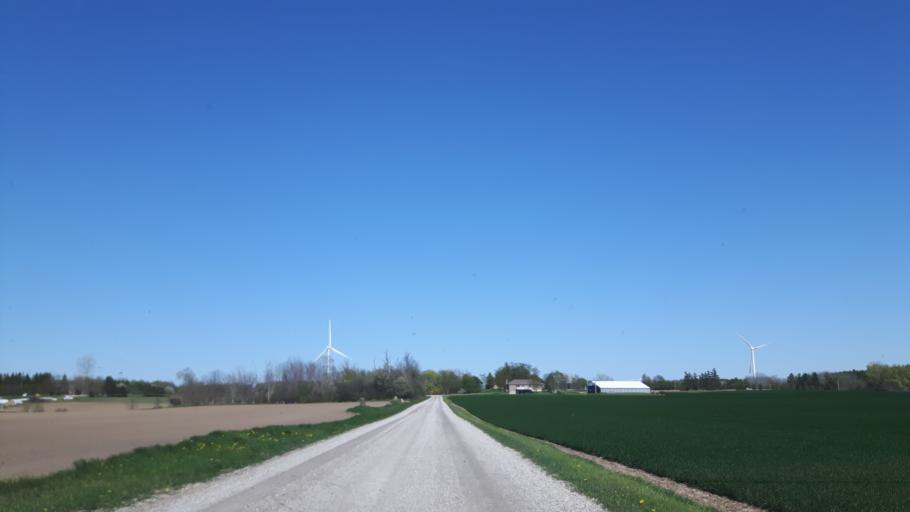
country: CA
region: Ontario
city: Bluewater
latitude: 43.5089
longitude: -81.6744
